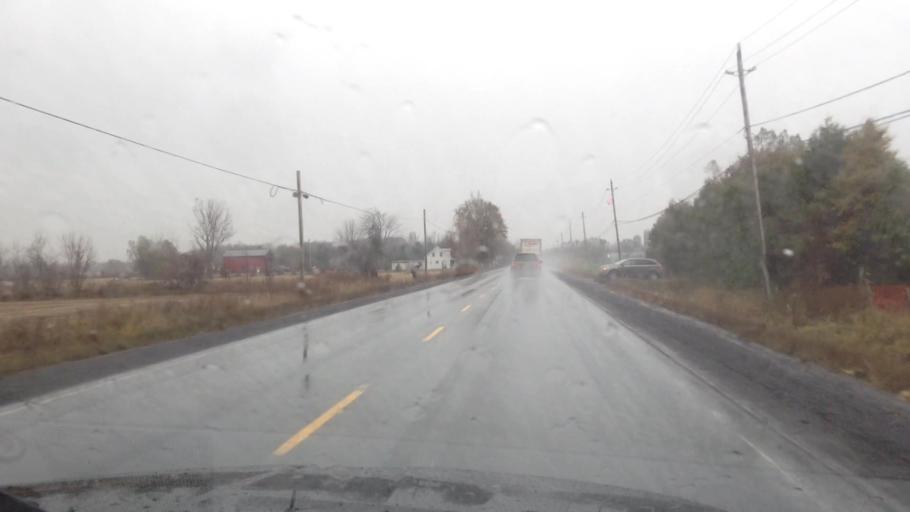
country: CA
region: Ontario
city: Bourget
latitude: 45.2827
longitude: -75.3182
